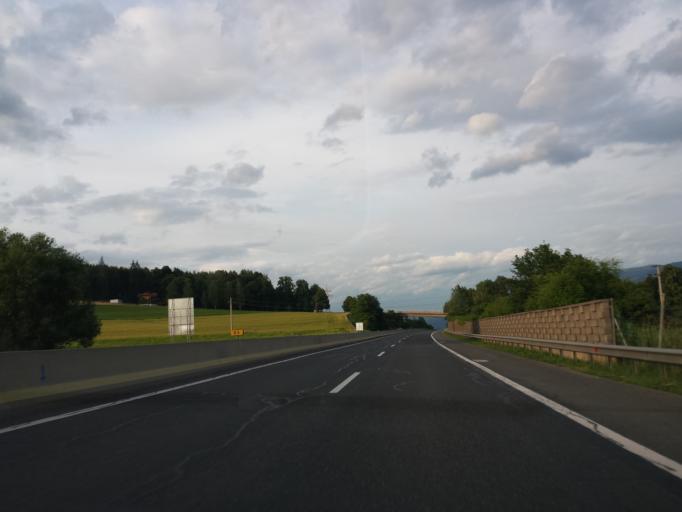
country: AT
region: Styria
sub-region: Politischer Bezirk Murtal
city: Knittelfeld
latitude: 47.2234
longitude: 14.8156
